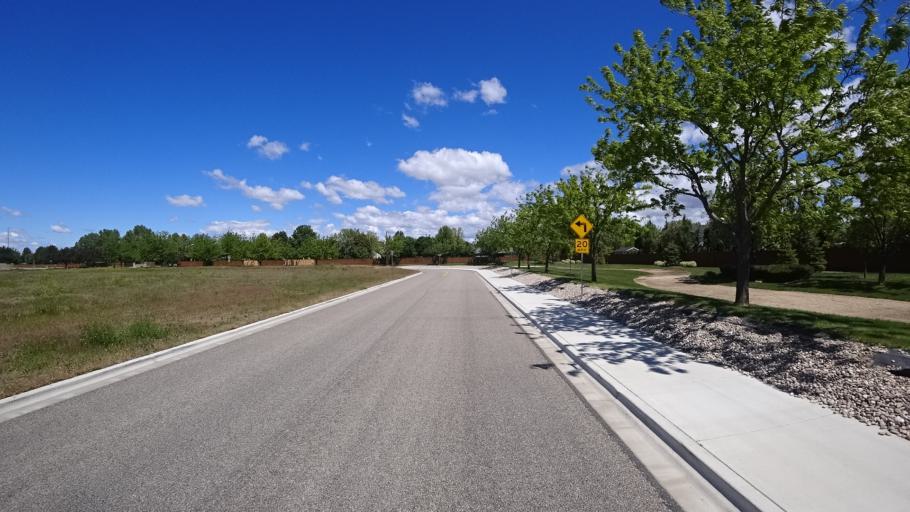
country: US
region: Idaho
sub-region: Ada County
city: Meridian
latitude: 43.6402
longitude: -116.3496
